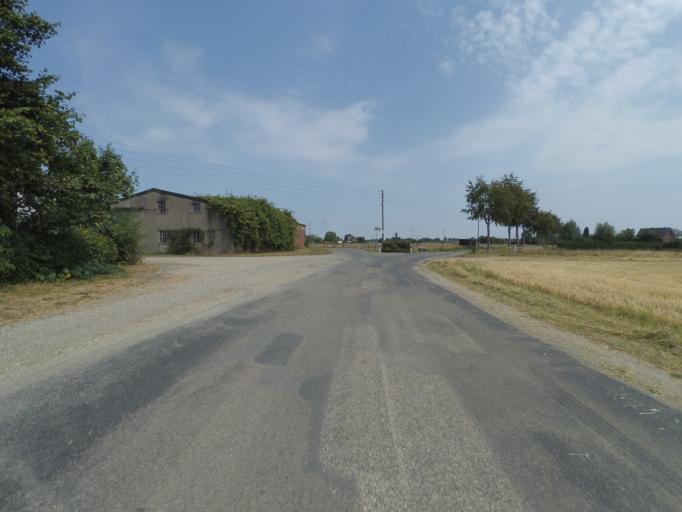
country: DE
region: North Rhine-Westphalia
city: Rees
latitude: 51.7775
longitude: 6.4375
